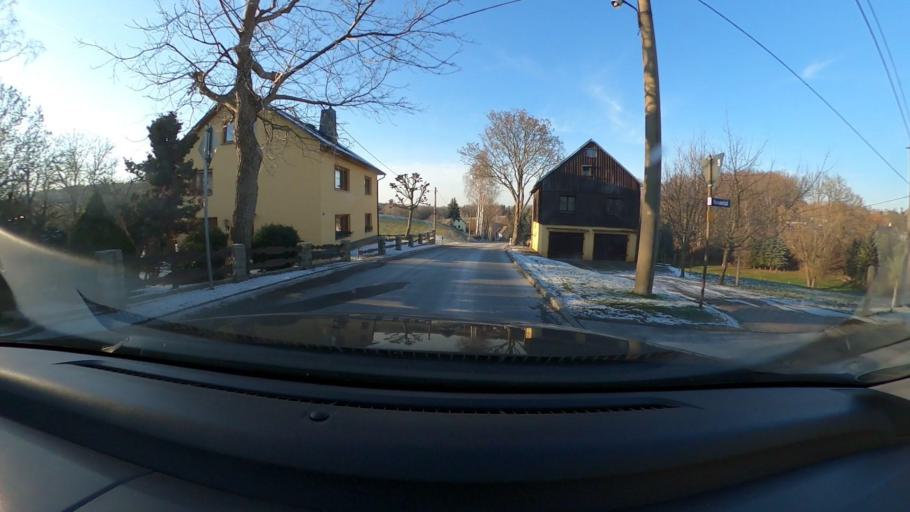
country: DE
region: Saxony
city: Frankenstein
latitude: 50.9385
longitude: 13.2104
